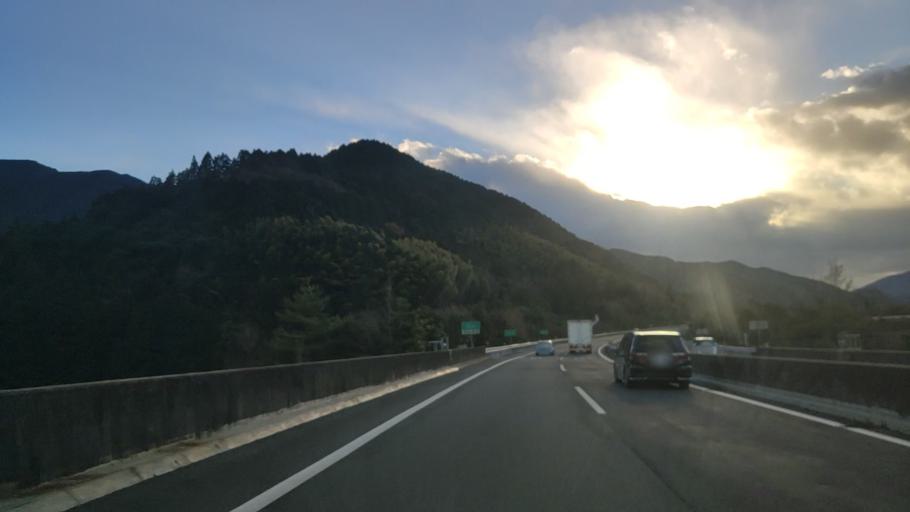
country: JP
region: Ehime
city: Saijo
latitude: 33.8664
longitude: 133.0573
